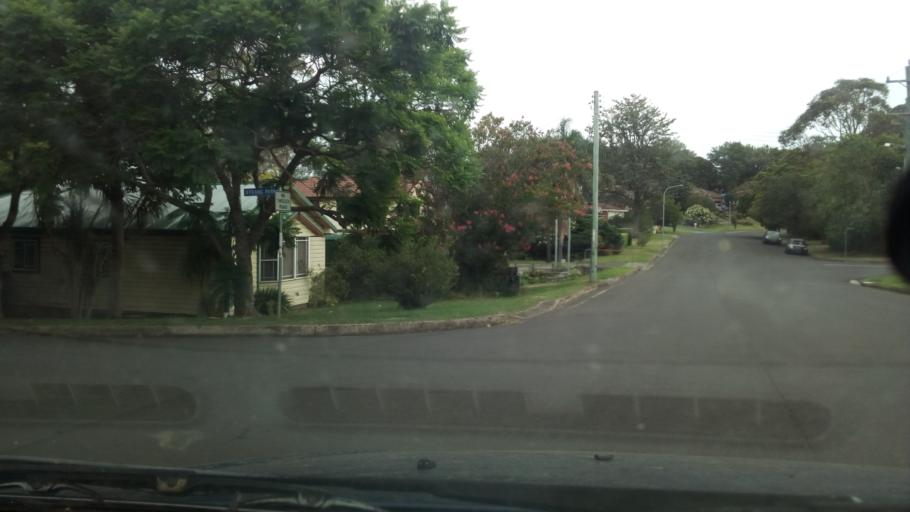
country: AU
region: New South Wales
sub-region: Wollongong
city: Keiraville
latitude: -34.4173
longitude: 150.8727
